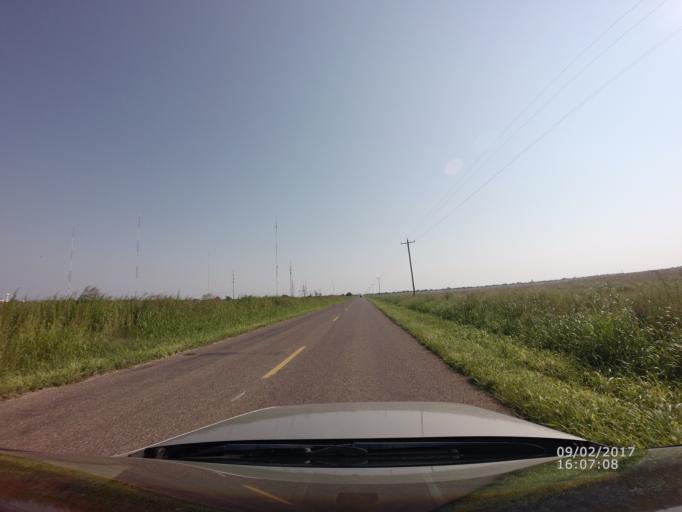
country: US
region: New Mexico
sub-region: Curry County
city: Clovis
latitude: 34.4432
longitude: -103.2141
